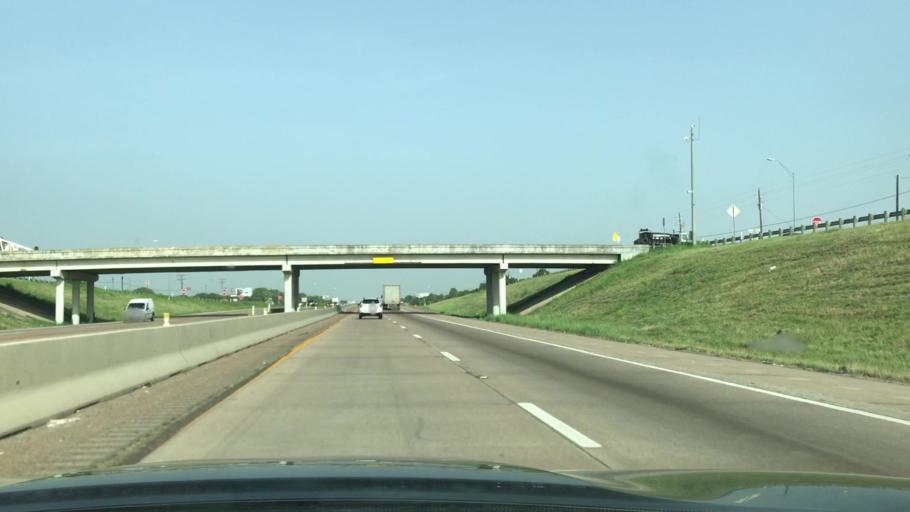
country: US
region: Texas
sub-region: Dallas County
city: Sunnyvale
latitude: 32.7805
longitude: -96.5358
